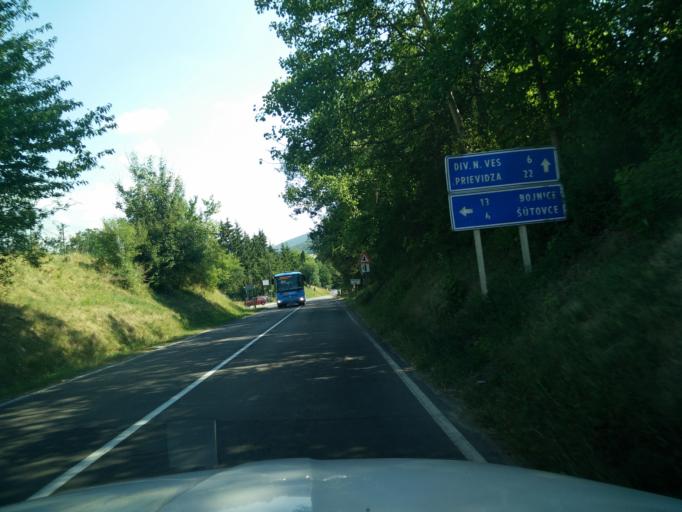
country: SK
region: Nitriansky
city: Novaky
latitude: 48.8018
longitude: 18.4764
